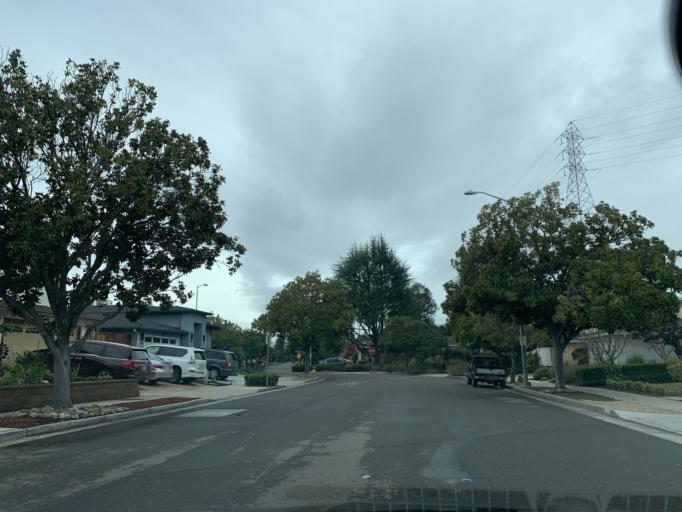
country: US
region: California
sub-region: Santa Clara County
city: Cupertino
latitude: 37.3302
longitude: -122.0552
